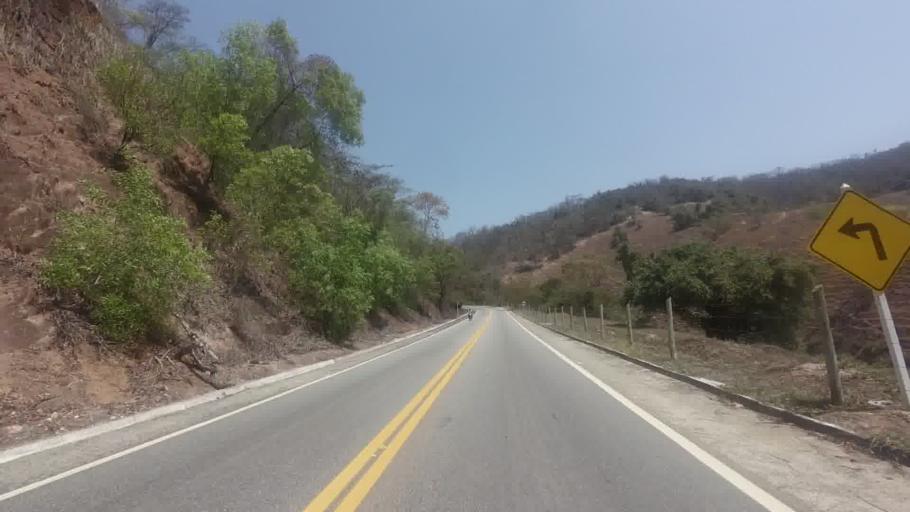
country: BR
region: Espirito Santo
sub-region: Cachoeiro De Itapemirim
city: Cachoeiro de Itapemirim
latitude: -20.8253
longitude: -41.2182
